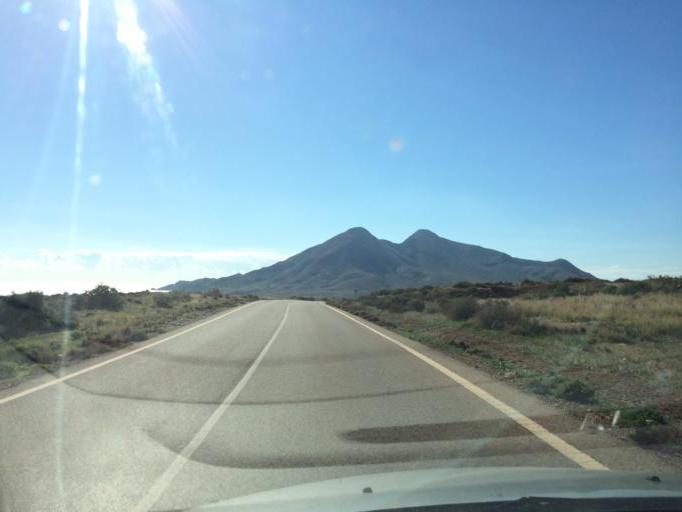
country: ES
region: Andalusia
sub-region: Provincia de Almeria
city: San Jose
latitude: 36.8175
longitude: -2.0609
